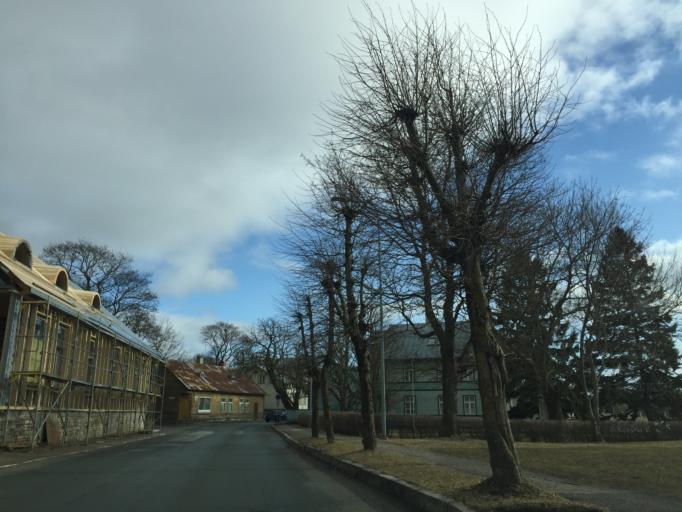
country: EE
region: Laeaene
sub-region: Haapsalu linn
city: Haapsalu
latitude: 58.9509
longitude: 23.5331
